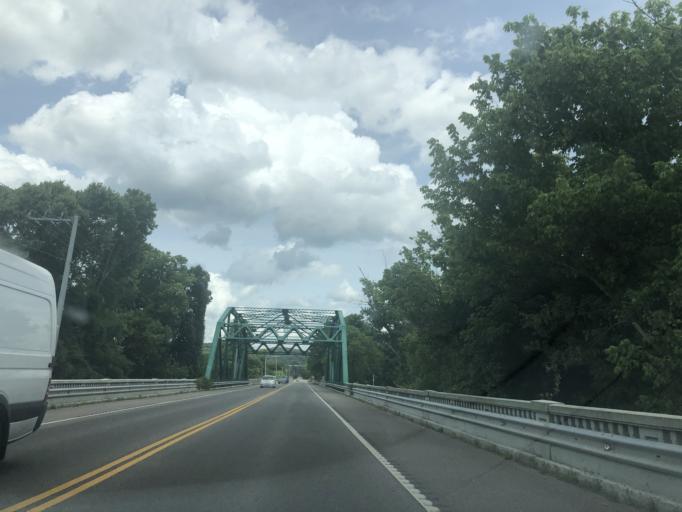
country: US
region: Tennessee
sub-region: Davidson County
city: Belle Meade
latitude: 36.0541
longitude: -86.9294
